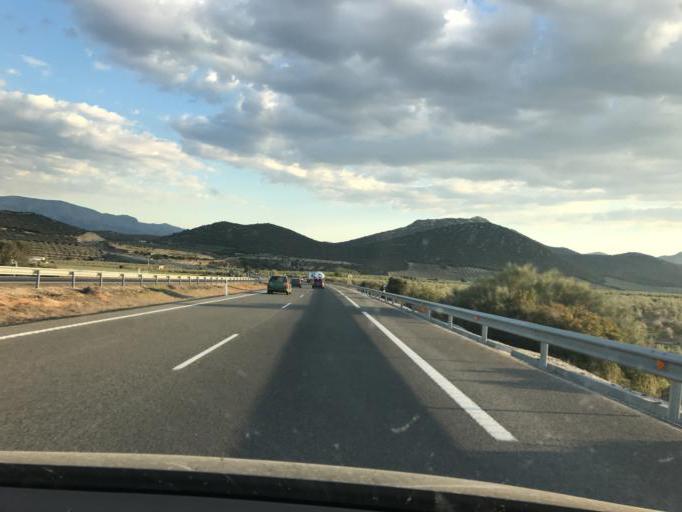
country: ES
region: Andalusia
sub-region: Provincia de Granada
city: Campotejar
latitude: 37.4589
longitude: -3.5630
